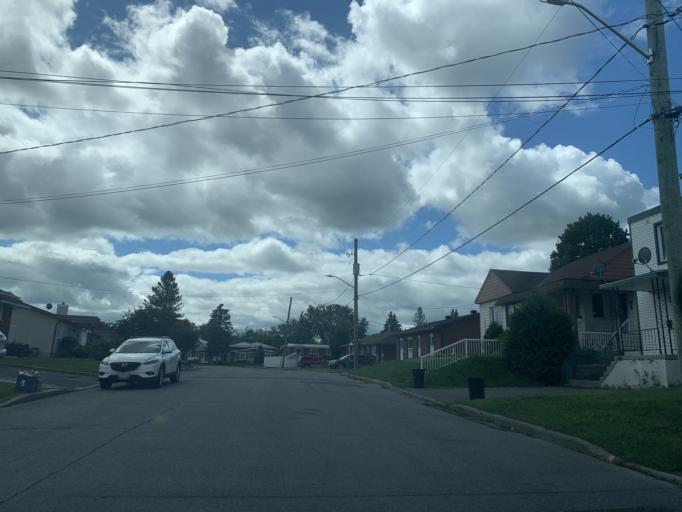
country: CA
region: Ontario
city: Hawkesbury
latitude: 45.6052
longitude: -74.6114
